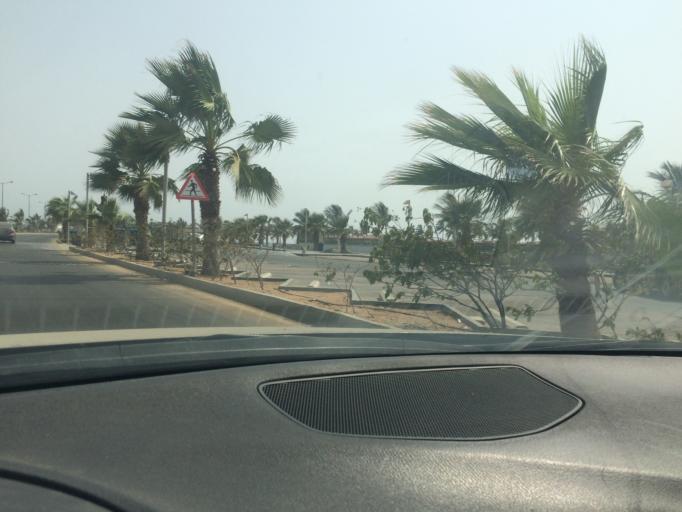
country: SA
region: Makkah
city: Jeddah
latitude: 21.5810
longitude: 39.1096
